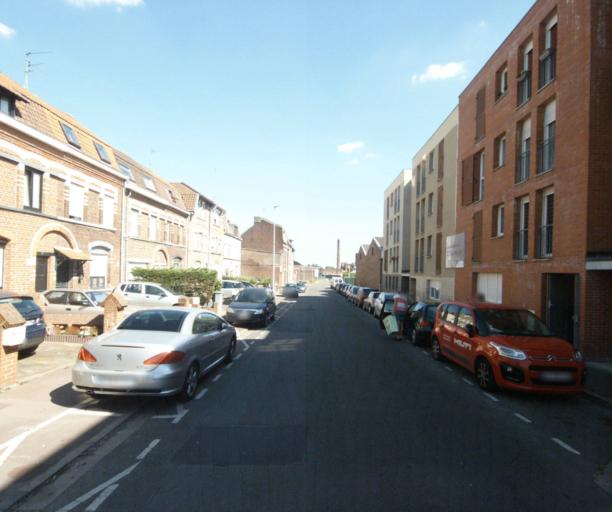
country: FR
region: Nord-Pas-de-Calais
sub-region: Departement du Nord
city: Tourcoing
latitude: 50.7286
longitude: 3.1783
